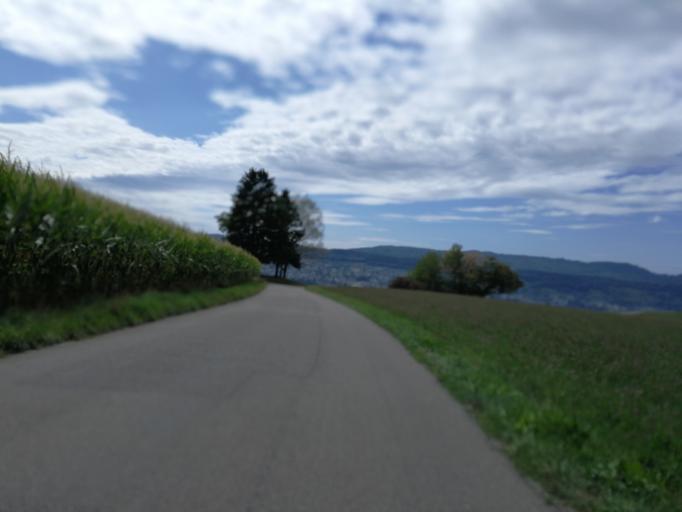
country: CH
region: Zurich
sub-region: Bezirk Meilen
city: Feldmeilen
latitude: 47.2810
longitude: 8.6340
